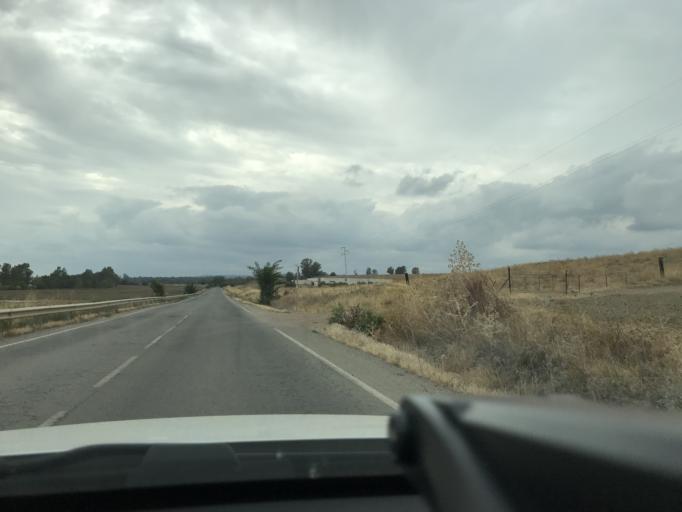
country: ES
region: Andalusia
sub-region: Provincia de Sevilla
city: Villanueva del Rio y Minas
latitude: 37.6354
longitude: -5.7140
